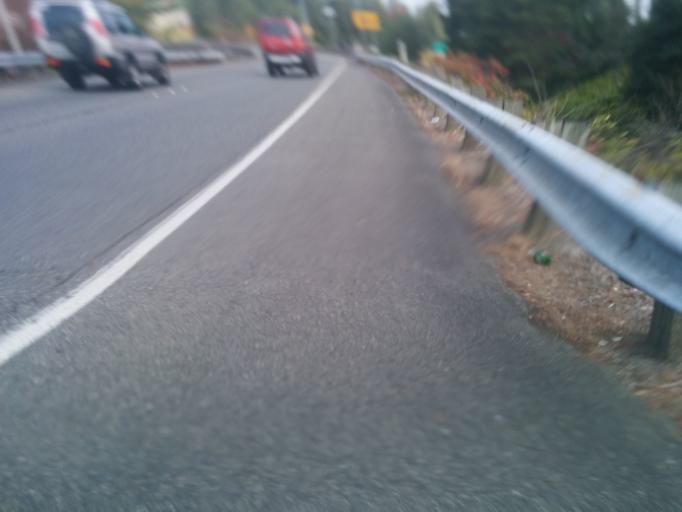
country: US
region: Washington
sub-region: King County
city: Shoreline
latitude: 47.6895
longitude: -122.3280
